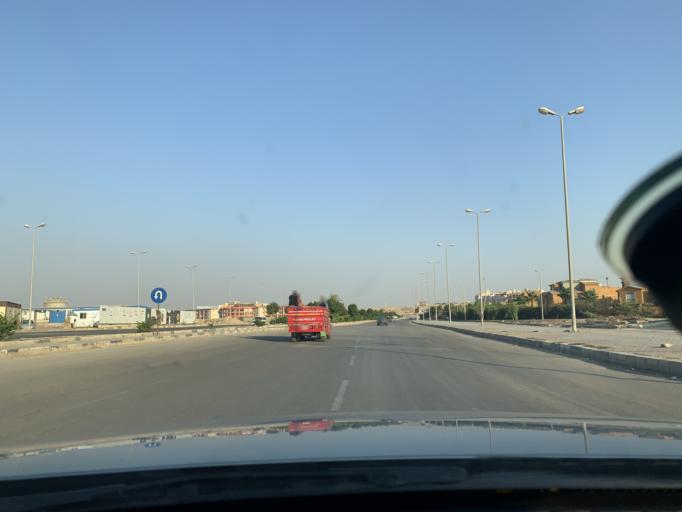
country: EG
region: Muhafazat al Qalyubiyah
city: Al Khankah
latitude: 30.0467
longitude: 31.5187
